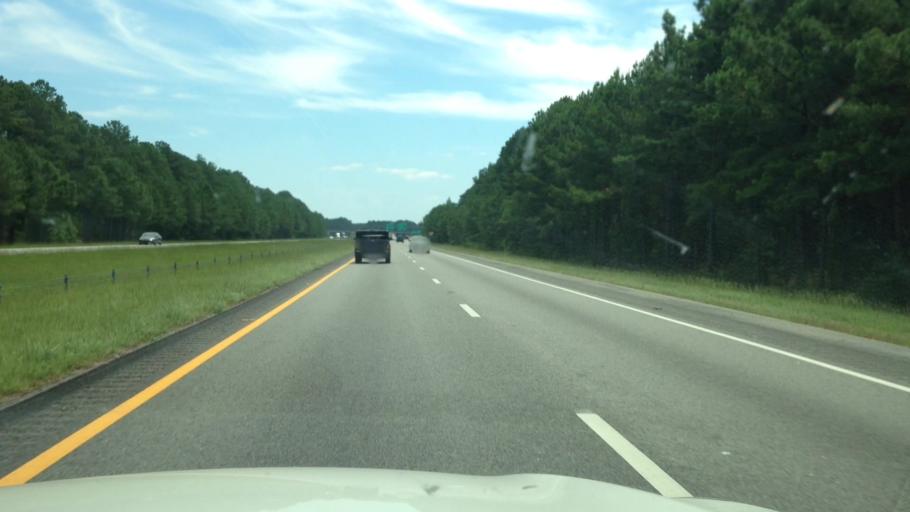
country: US
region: South Carolina
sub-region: Florence County
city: Florence
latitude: 34.1997
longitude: -79.8592
